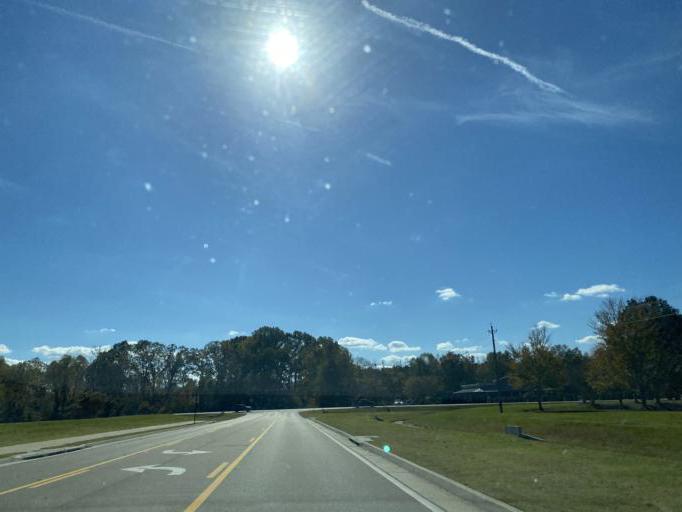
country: US
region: Mississippi
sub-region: Madison County
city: Madison
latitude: 32.4591
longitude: -90.1276
